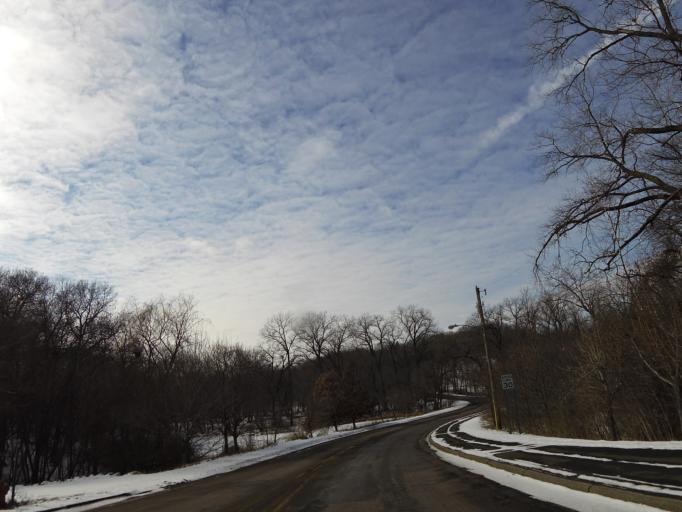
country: US
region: Minnesota
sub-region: Scott County
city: Savage
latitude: 44.8085
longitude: -93.4015
